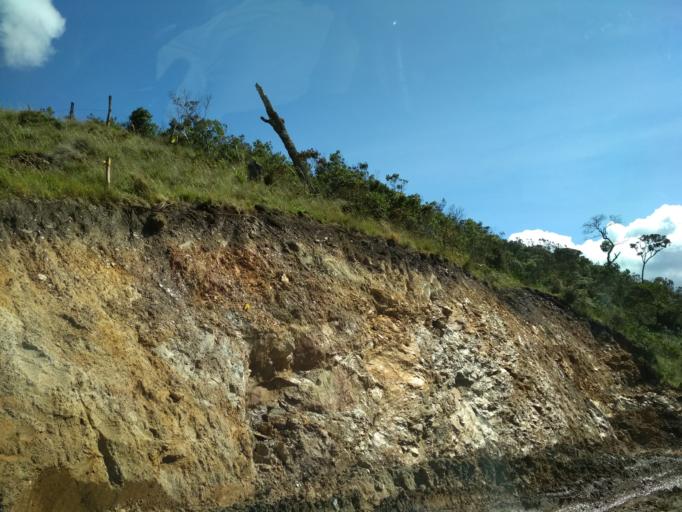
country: CO
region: Cauca
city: Silvia
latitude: 2.6942
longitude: -76.3315
